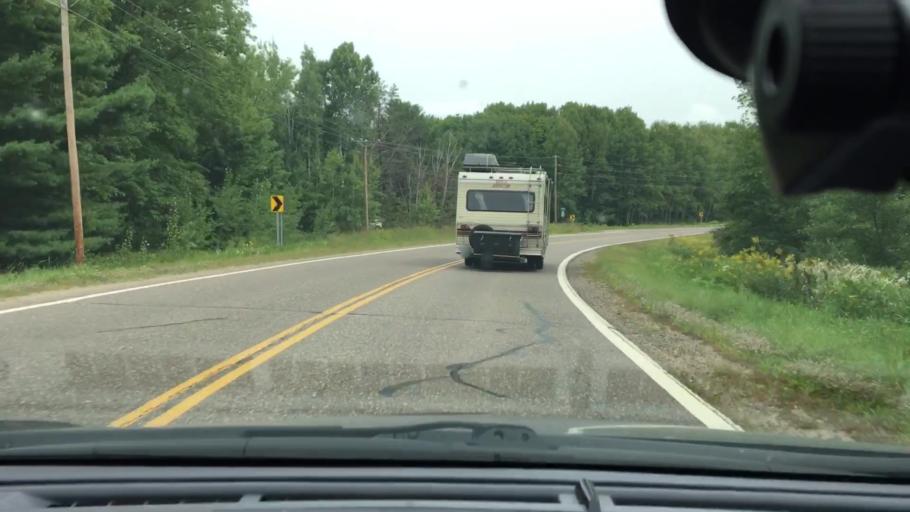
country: US
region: Minnesota
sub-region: Aitkin County
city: Aitkin
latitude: 46.4042
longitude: -93.7924
